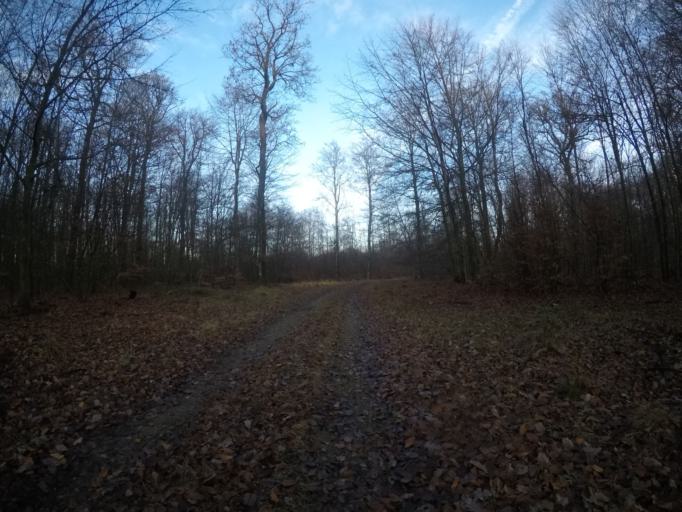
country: BE
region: Wallonia
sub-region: Province du Luxembourg
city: Habay-la-Vieille
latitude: 49.7503
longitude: 5.6720
